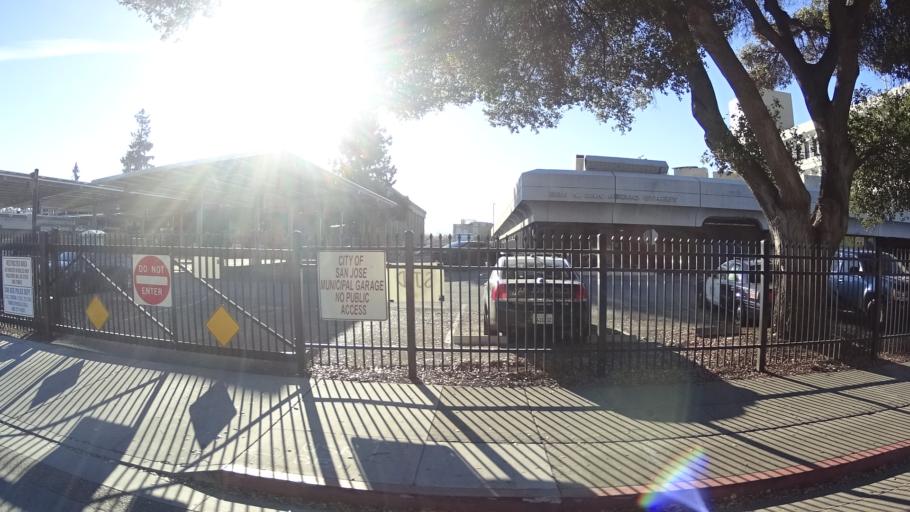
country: US
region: California
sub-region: Santa Clara County
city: San Jose
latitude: 37.3501
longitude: -121.9046
